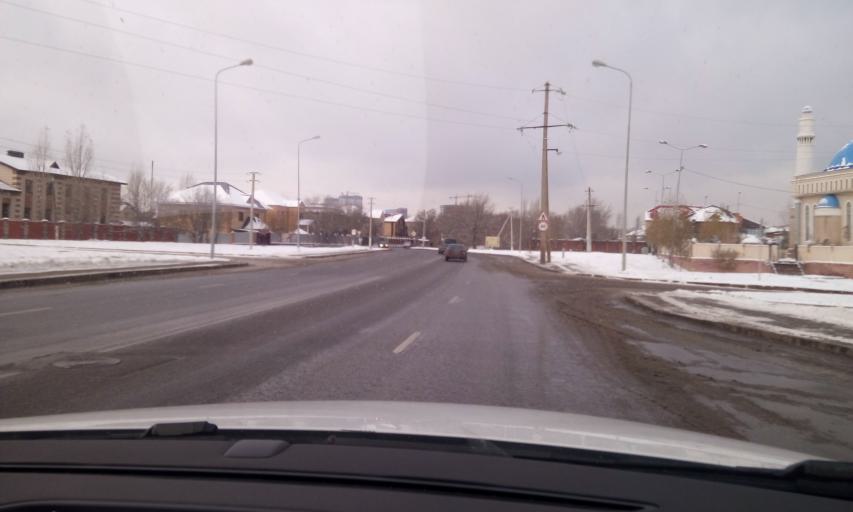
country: KZ
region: Astana Qalasy
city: Astana
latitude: 51.1382
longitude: 71.4347
